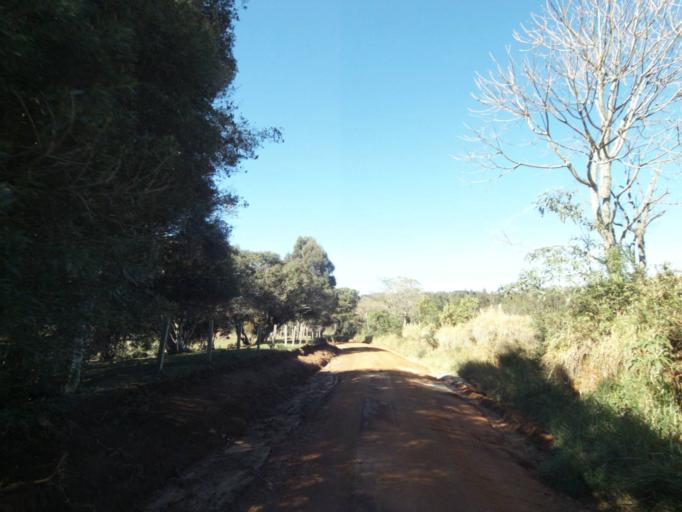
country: BR
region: Parana
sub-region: Tibagi
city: Tibagi
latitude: -24.5885
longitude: -50.2621
